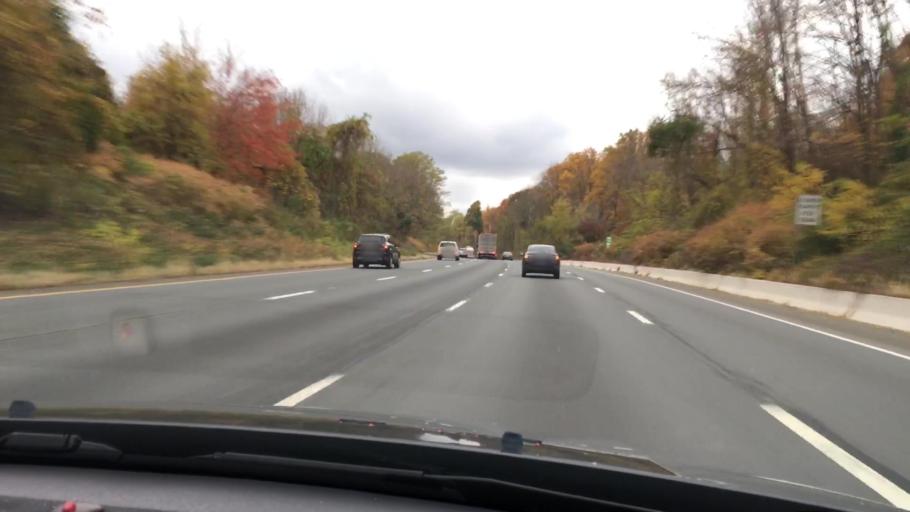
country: US
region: New Jersey
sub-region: Morris County
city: Morristown
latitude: 40.7611
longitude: -74.5177
